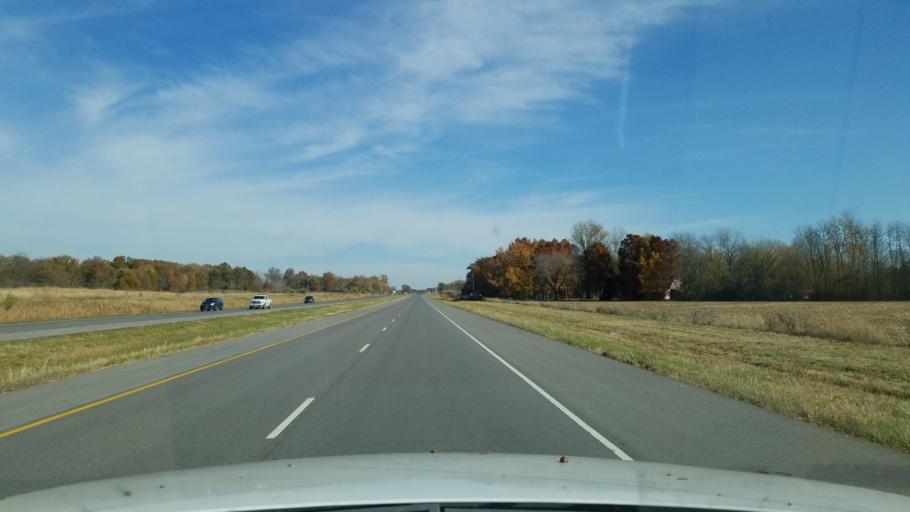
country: US
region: Illinois
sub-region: Saline County
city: Eldorado
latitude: 37.7827
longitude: -88.4910
